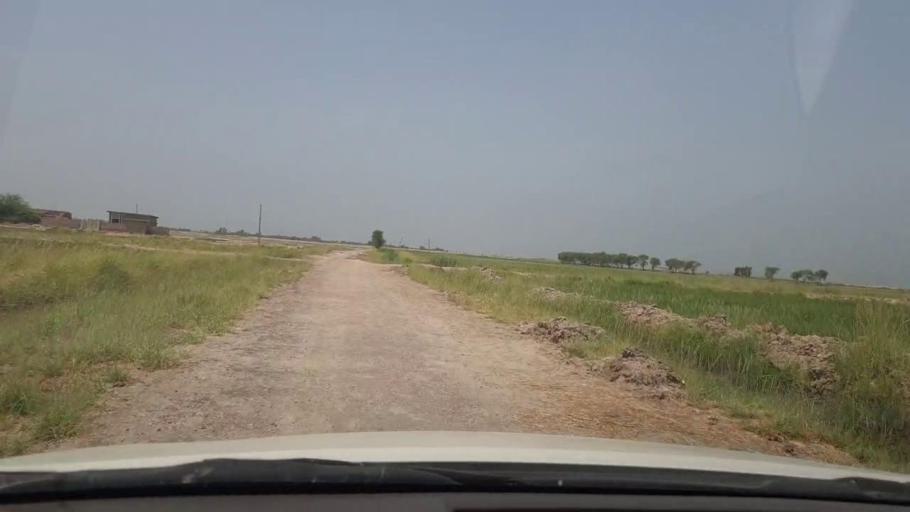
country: PK
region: Sindh
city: Shikarpur
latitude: 28.0239
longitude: 68.6073
